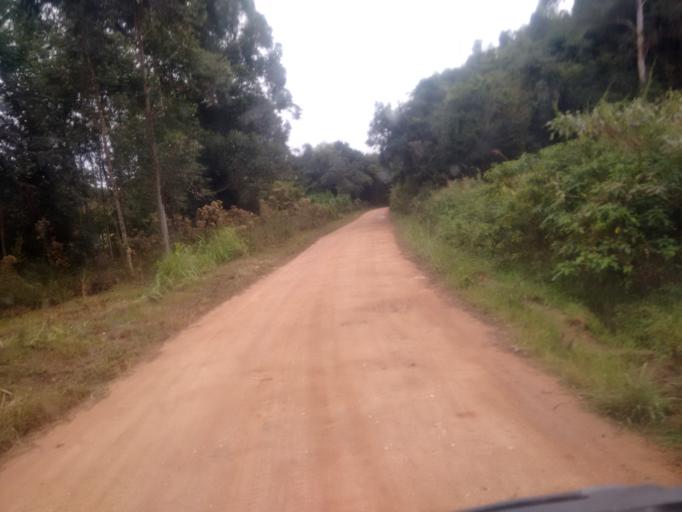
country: BR
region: Rio Grande do Sul
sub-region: Camaqua
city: Camaqua
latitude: -30.7225
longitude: -51.8705
